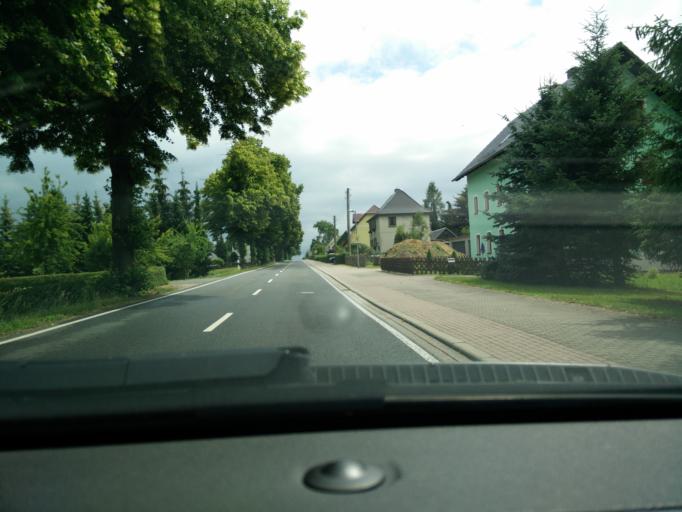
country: DE
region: Saxony
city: Bad Lausick
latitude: 51.1287
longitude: 12.6577
